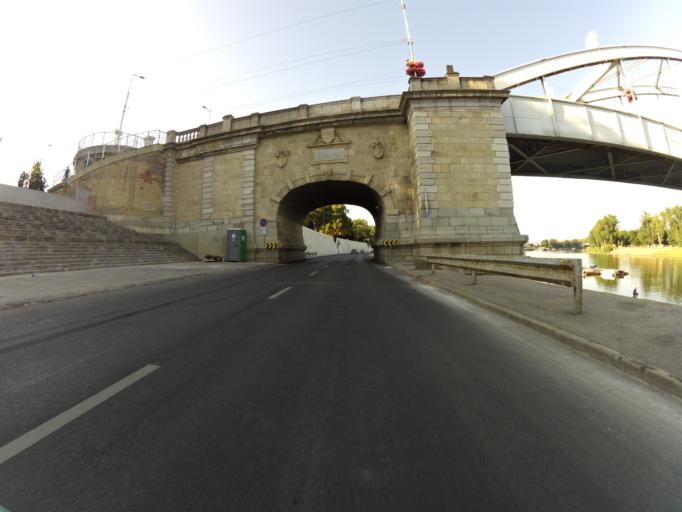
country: HU
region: Csongrad
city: Szeged
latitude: 46.2508
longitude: 20.1522
